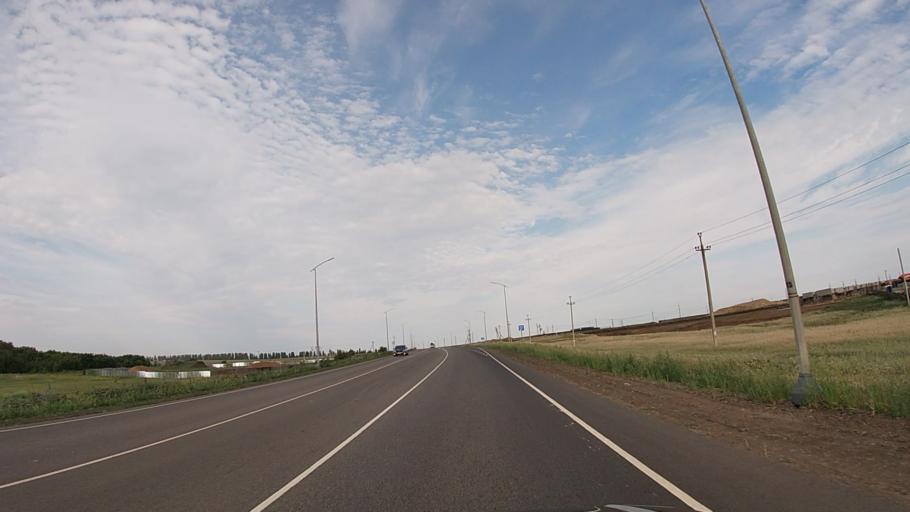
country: RU
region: Belgorod
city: Severnyy
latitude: 50.6673
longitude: 36.5452
